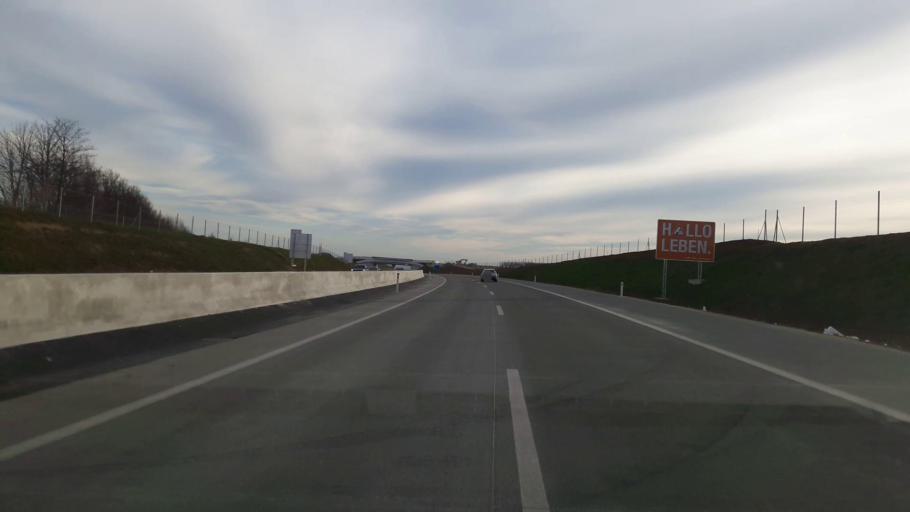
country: AT
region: Lower Austria
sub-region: Politischer Bezirk Mistelbach
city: Herrnbaumgarten
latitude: 48.6998
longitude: 16.6520
